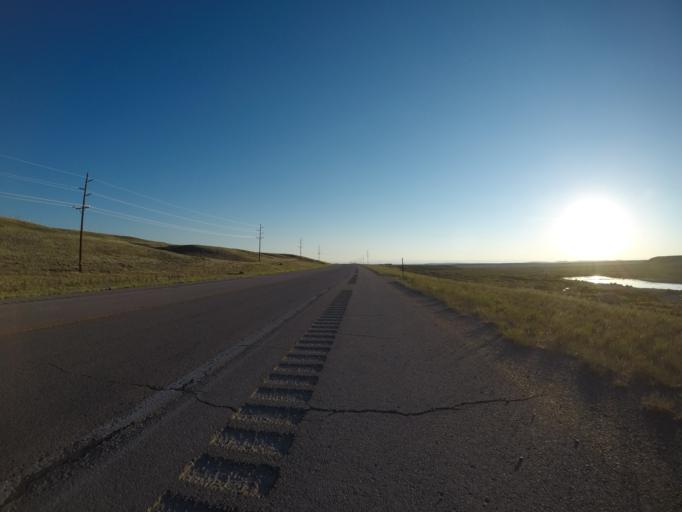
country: US
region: Wyoming
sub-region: Sublette County
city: Marbleton
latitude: 42.5709
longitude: -110.0958
